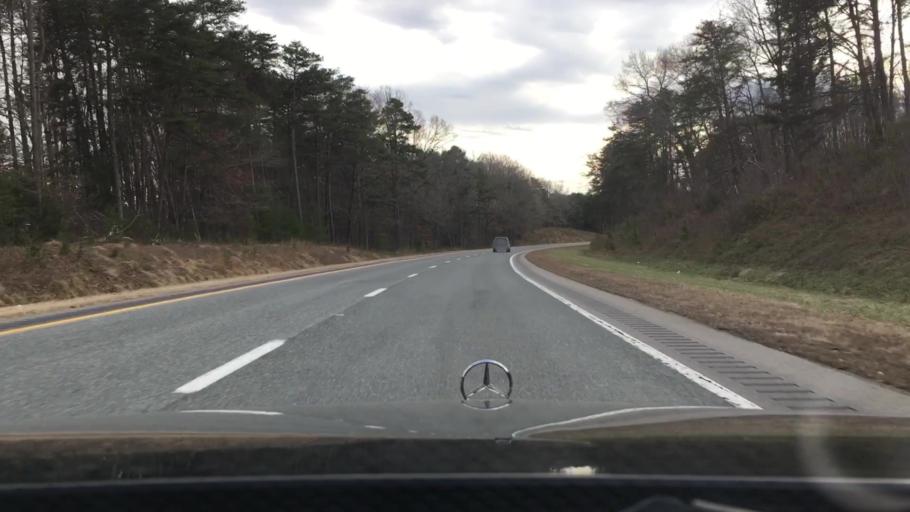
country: US
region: Virginia
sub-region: Pittsylvania County
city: Gretna
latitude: 36.9307
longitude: -79.3761
